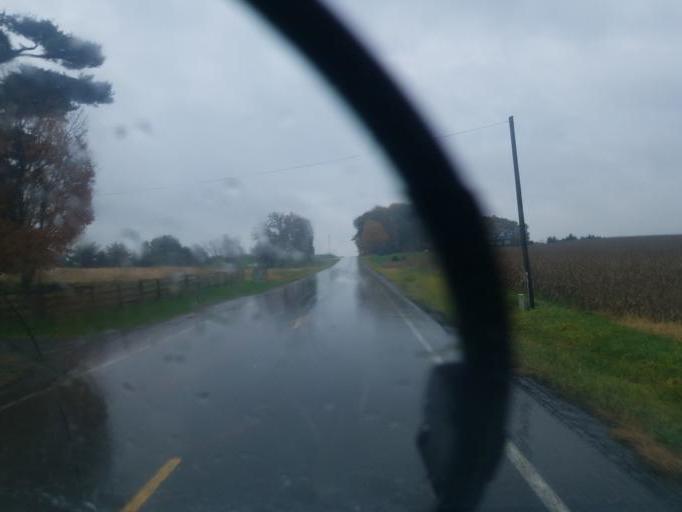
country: US
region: Ohio
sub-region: Licking County
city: Utica
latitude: 40.2501
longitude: -82.3243
